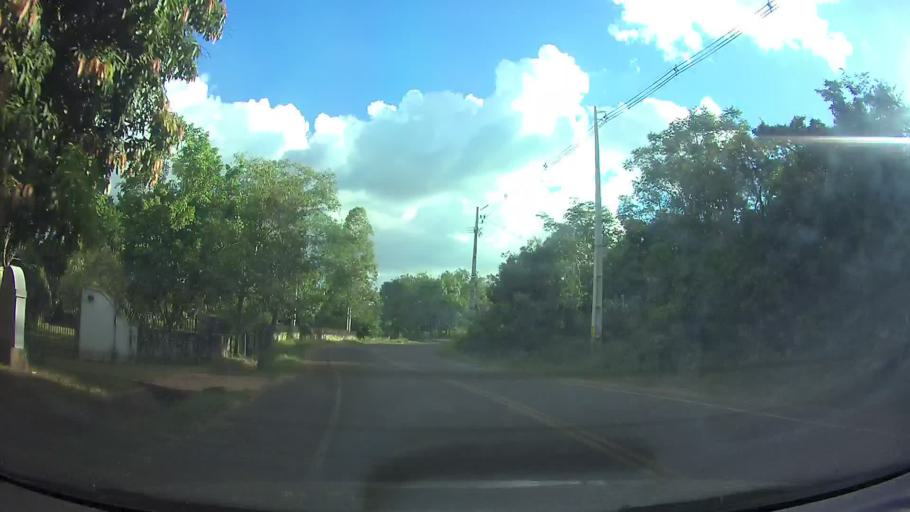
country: PY
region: Cordillera
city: Altos
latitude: -25.2472
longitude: -57.2349
